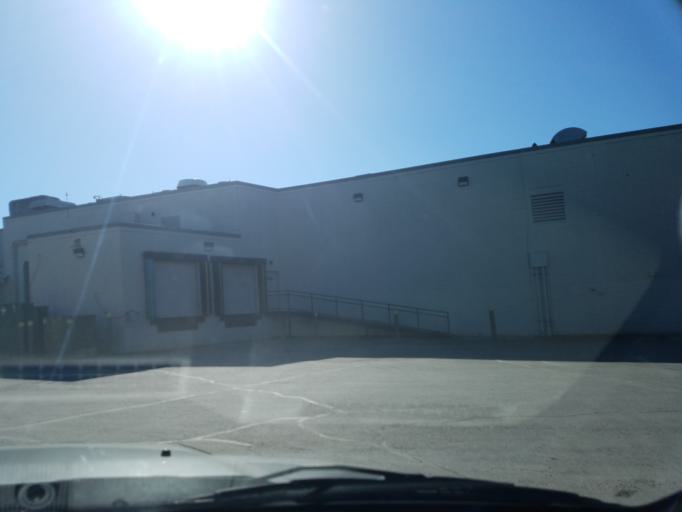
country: US
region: Alaska
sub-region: Anchorage Municipality
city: Elmendorf Air Force Base
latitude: 61.1971
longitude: -149.7366
